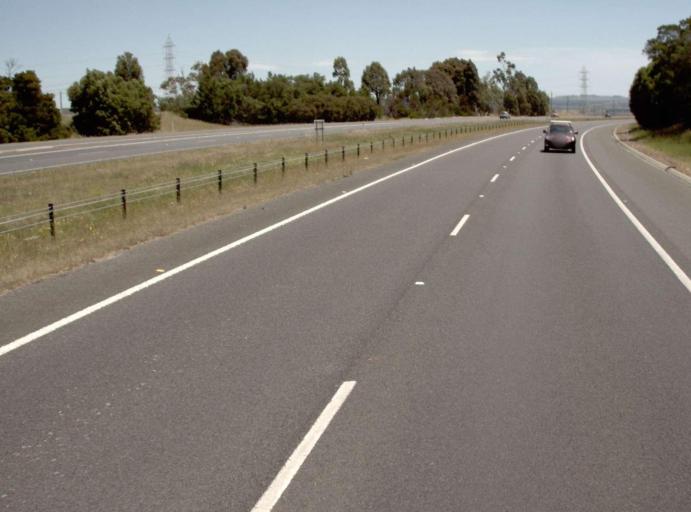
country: AU
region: Victoria
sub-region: Latrobe
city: Morwell
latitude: -38.2427
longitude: 146.4035
